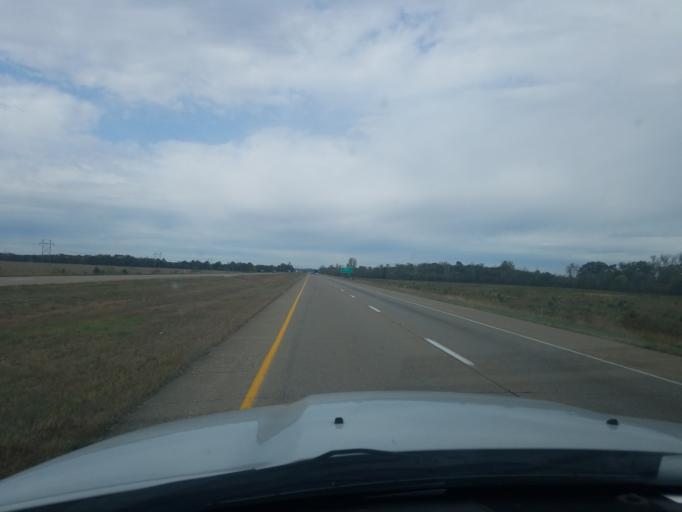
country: US
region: Indiana
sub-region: Vanderburgh County
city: Melody Hill
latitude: 38.0658
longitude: -87.4756
